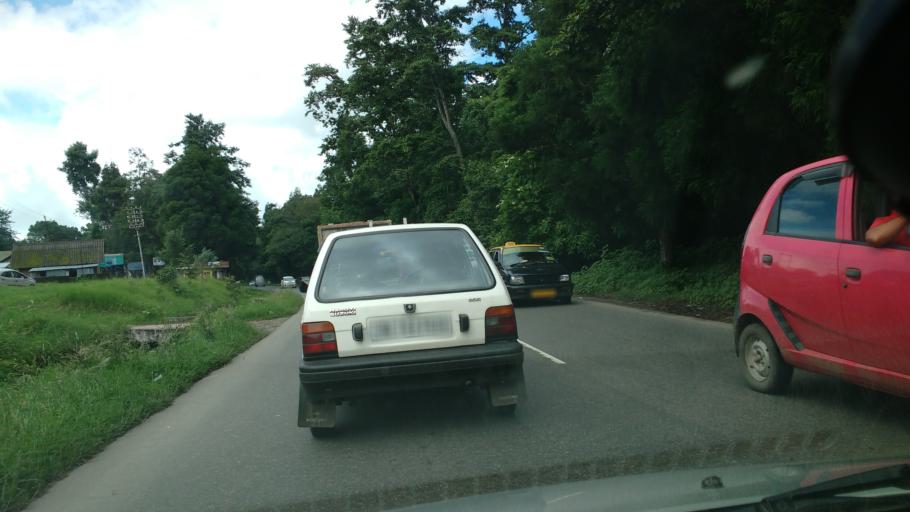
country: IN
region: Meghalaya
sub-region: East Khasi Hills
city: Shillong
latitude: 25.5516
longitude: 91.8433
